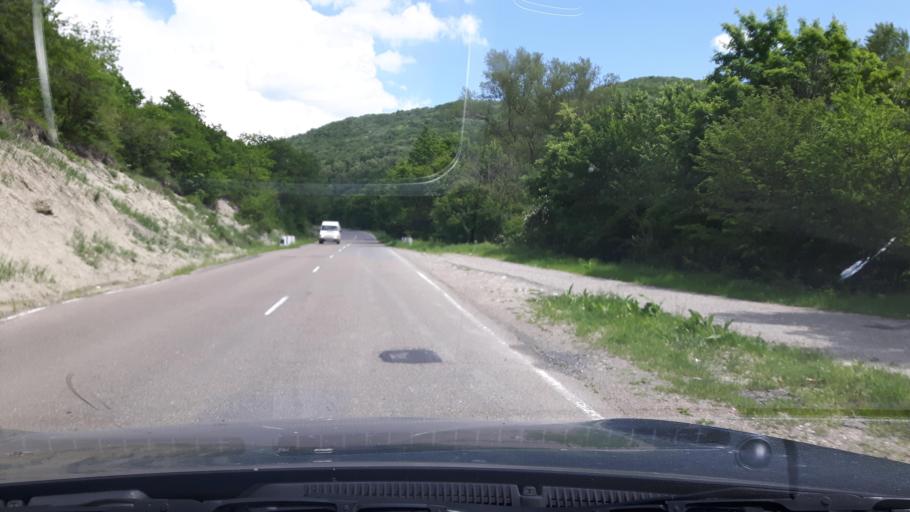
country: GE
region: Kakheti
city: Akhmet'a
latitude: 41.8641
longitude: 45.1520
